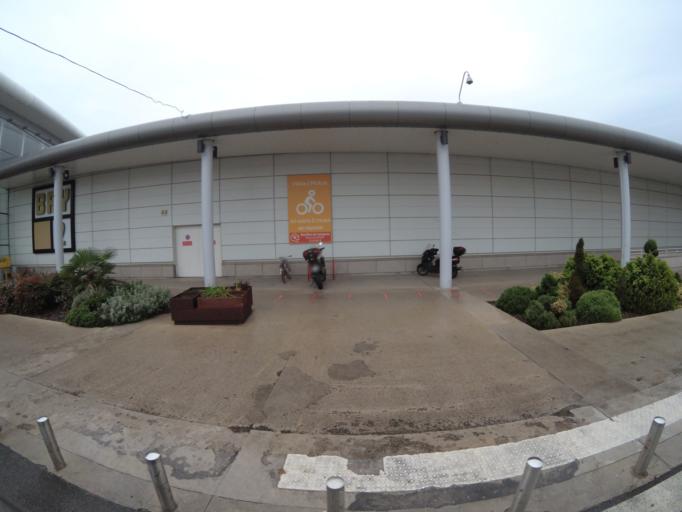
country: FR
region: Ile-de-France
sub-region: Departement de Seine-et-Marne
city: Collegien
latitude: 48.8381
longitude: 2.6623
